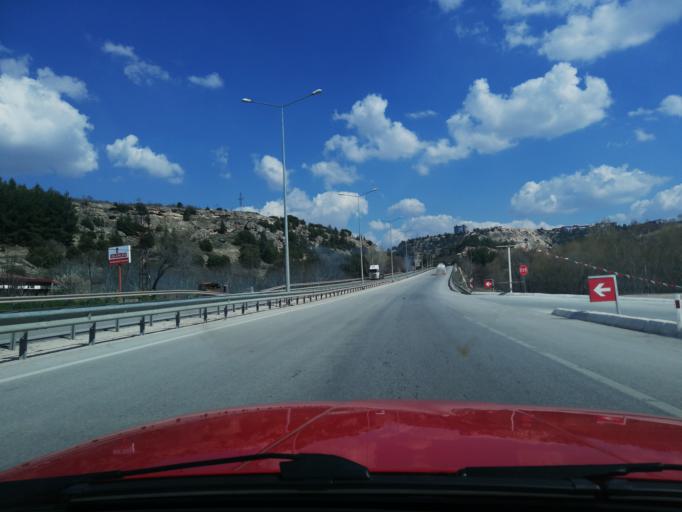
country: TR
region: Burdur
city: Burdur
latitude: 37.6986
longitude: 30.3254
